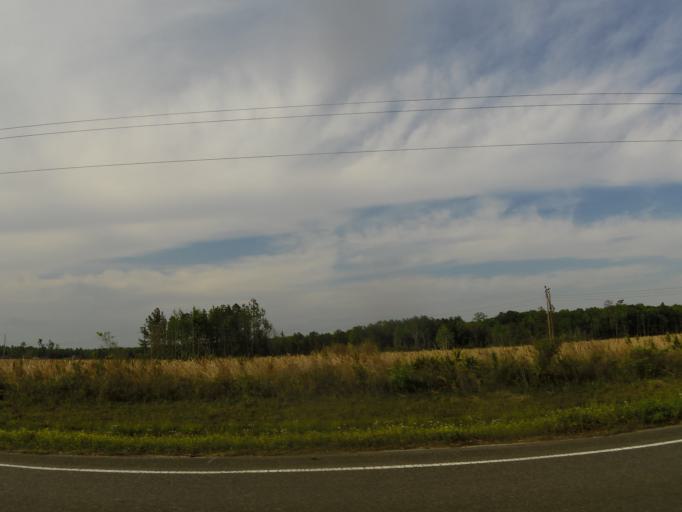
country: US
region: Florida
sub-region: Nassau County
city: Yulee
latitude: 30.6887
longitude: -81.6679
